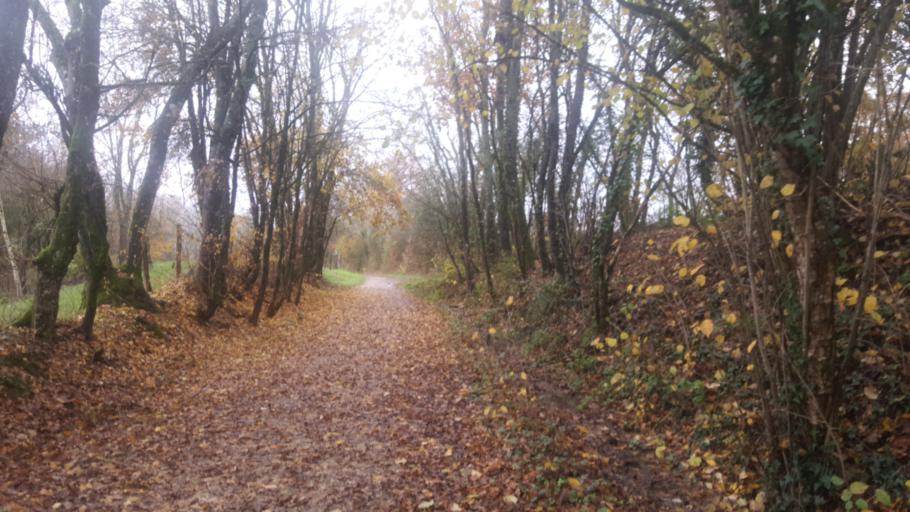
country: FR
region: Poitou-Charentes
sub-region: Departement des Deux-Sevres
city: Melle
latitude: 46.2319
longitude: -0.1469
